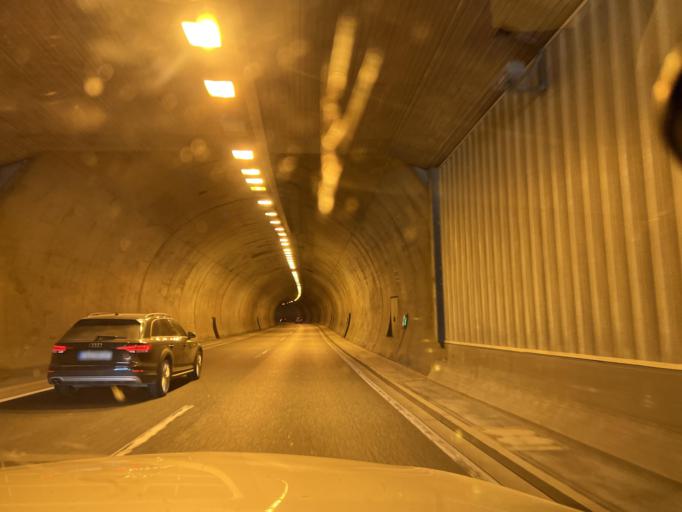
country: DE
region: North Rhine-Westphalia
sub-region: Regierungsbezirk Arnsberg
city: Siegen
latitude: 50.8720
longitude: 8.0074
